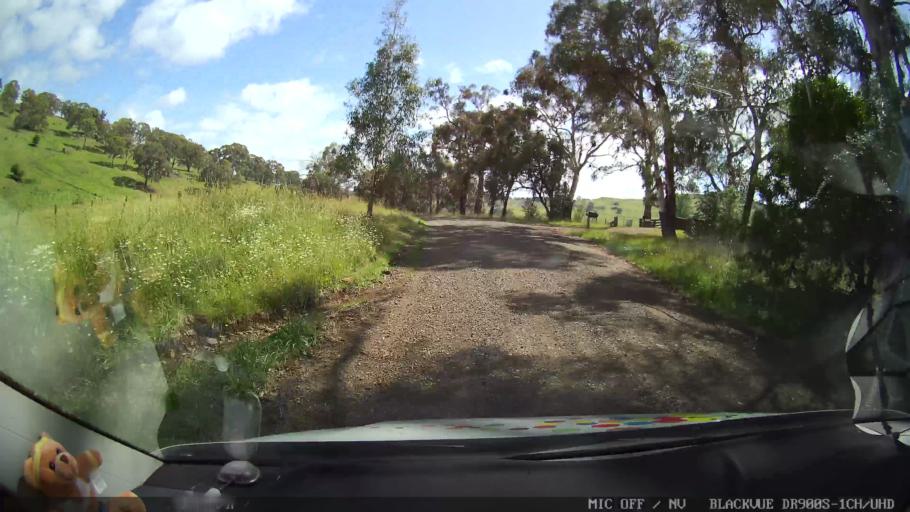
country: AU
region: New South Wales
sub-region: Guyra
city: Guyra
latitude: -29.9854
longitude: 151.6937
